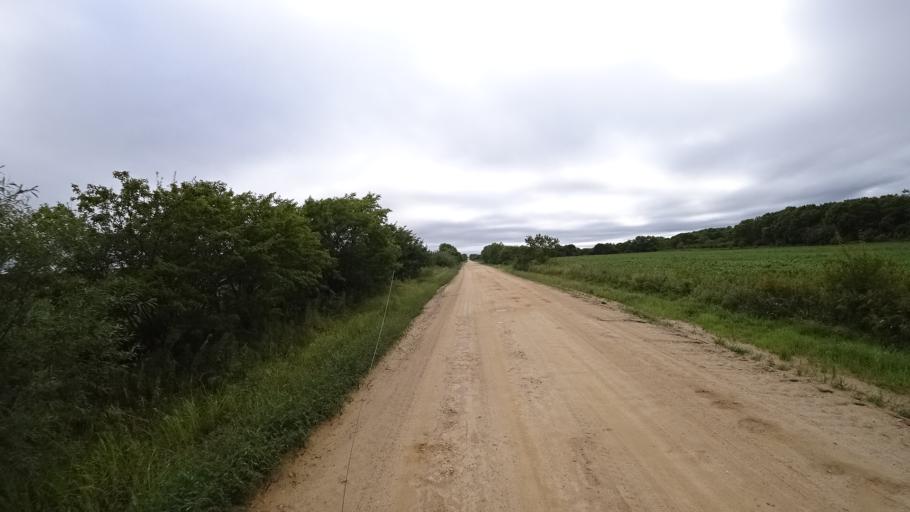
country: RU
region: Primorskiy
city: Rettikhovka
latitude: 44.1194
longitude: 132.6321
